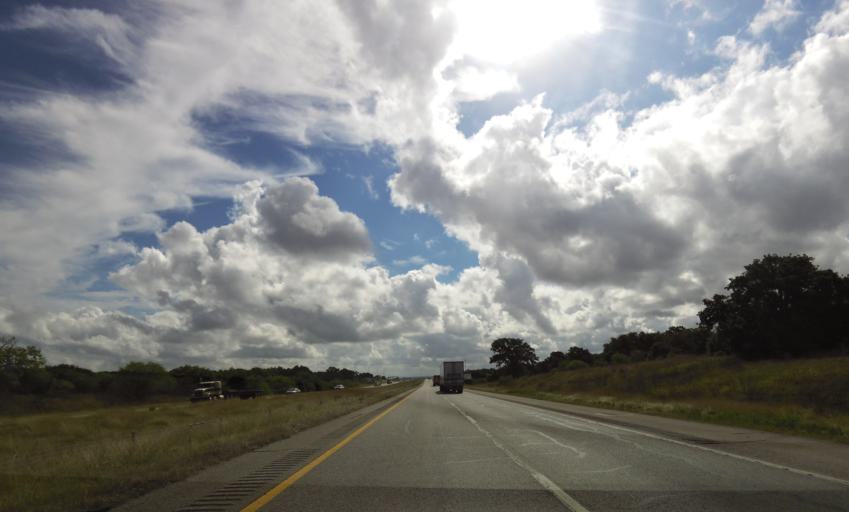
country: US
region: Texas
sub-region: Caldwell County
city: Luling
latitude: 29.6226
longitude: -97.7785
